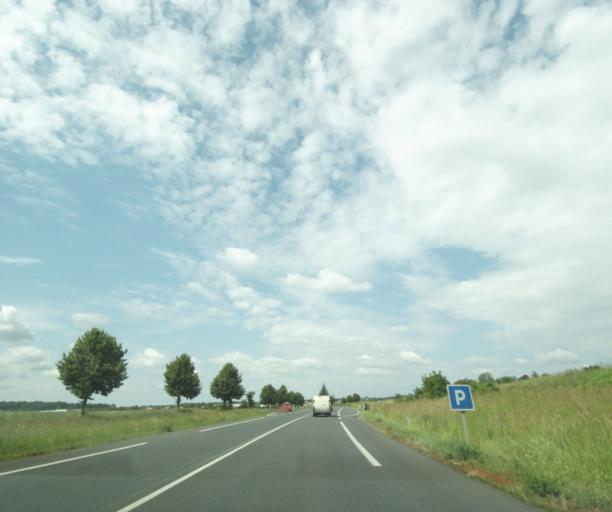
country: FR
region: Pays de la Loire
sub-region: Departement de Maine-et-Loire
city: Distre
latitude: 47.2222
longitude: -0.1172
